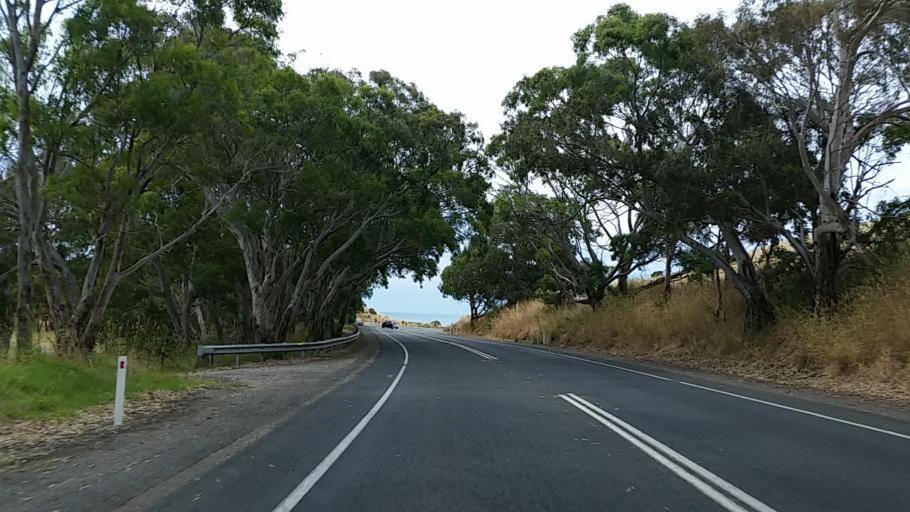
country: AU
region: South Australia
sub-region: Onkaparinga
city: Aldinga
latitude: -35.3672
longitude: 138.4578
